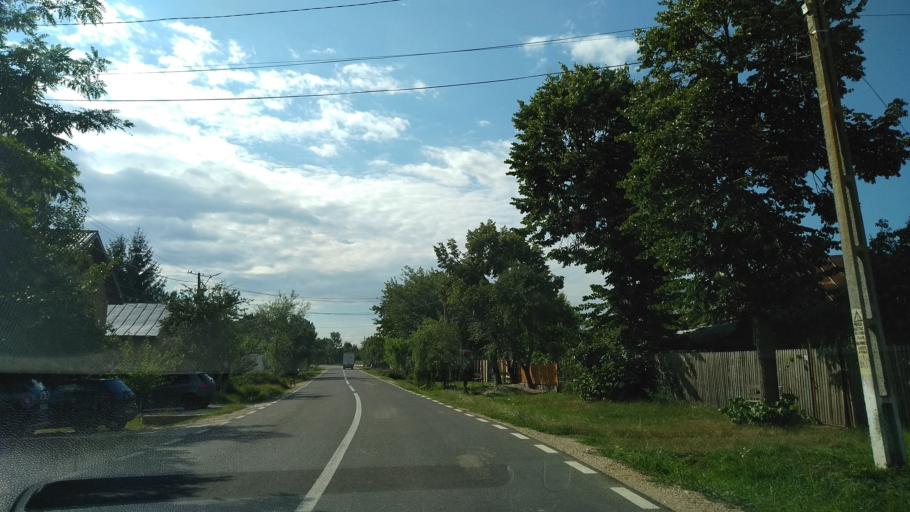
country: RO
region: Dambovita
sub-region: Comuna Uliesti
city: Uliesti
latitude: 44.5963
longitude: 25.4030
